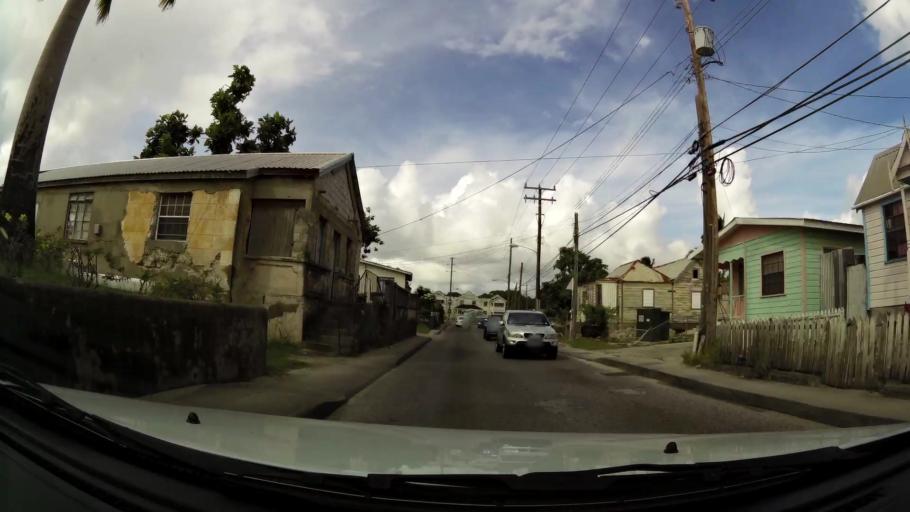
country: BB
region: Saint Michael
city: Bridgetown
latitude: 13.1290
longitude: -59.6066
